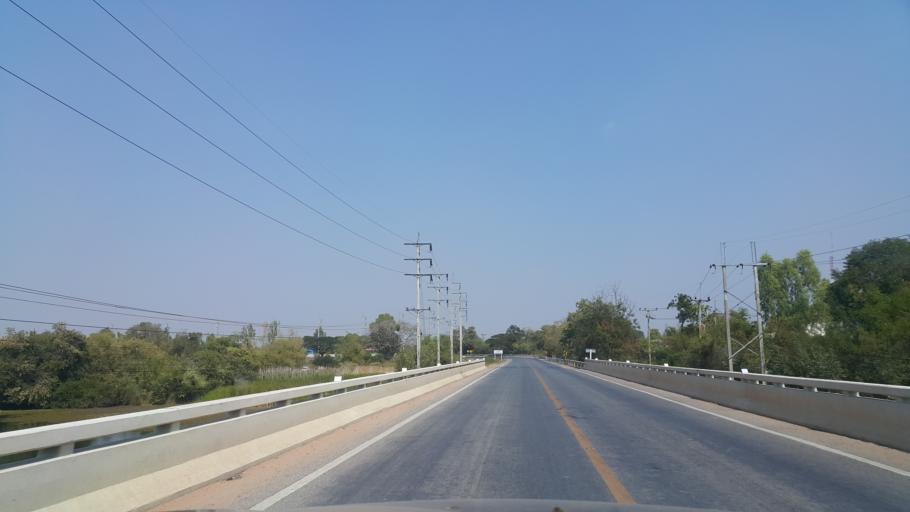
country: TH
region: Nakhon Ratchasima
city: Prathai
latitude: 15.5022
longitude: 102.7537
